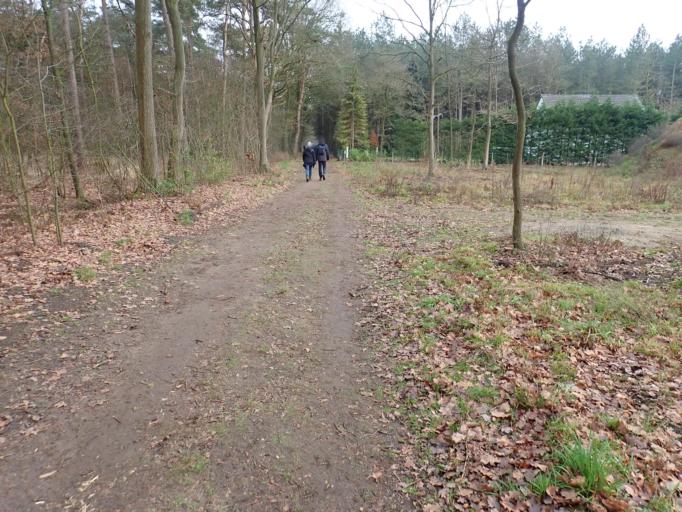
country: BE
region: Flanders
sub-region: Provincie Antwerpen
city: Zandhoven
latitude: 51.2273
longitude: 4.6317
